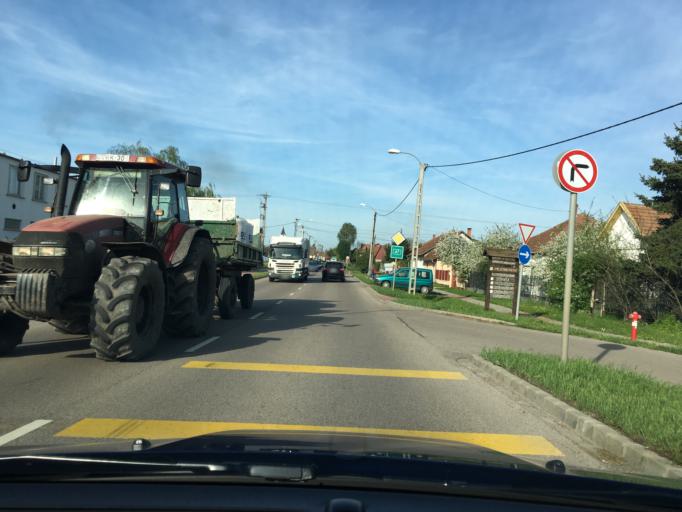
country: HU
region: Bekes
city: Mezobereny
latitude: 46.8130
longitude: 21.0168
